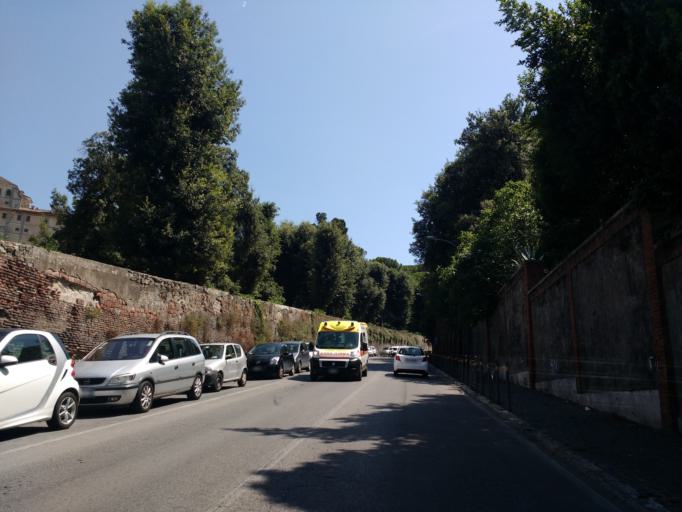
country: IT
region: Latium
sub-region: Citta metropolitana di Roma Capitale
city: Armetta
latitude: 41.8048
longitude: 12.6805
